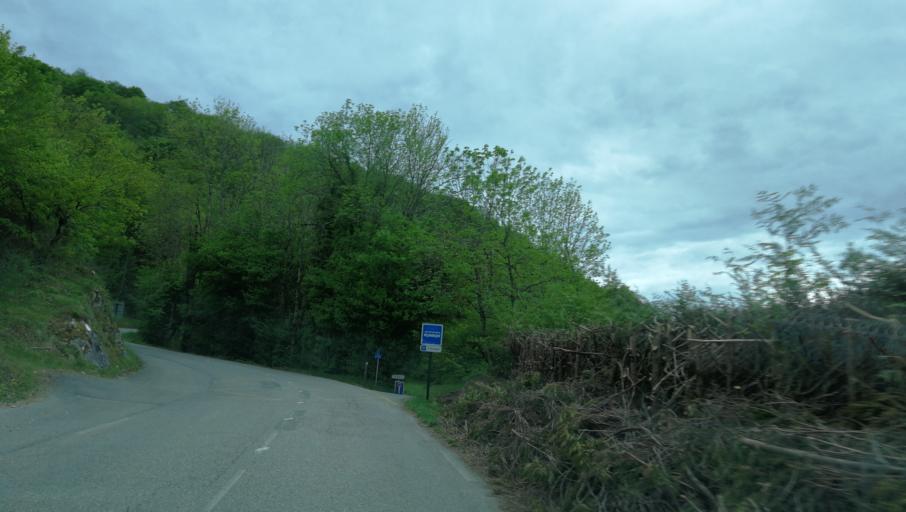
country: FR
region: Rhone-Alpes
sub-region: Departement de la Savoie
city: Chatillon
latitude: 45.7849
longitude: 5.8230
